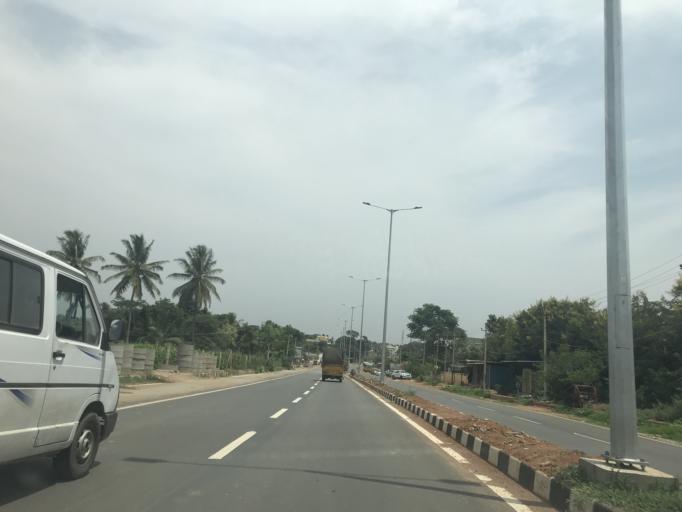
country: IN
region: Karnataka
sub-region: Bangalore Urban
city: Yelahanka
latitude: 13.1413
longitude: 77.6712
